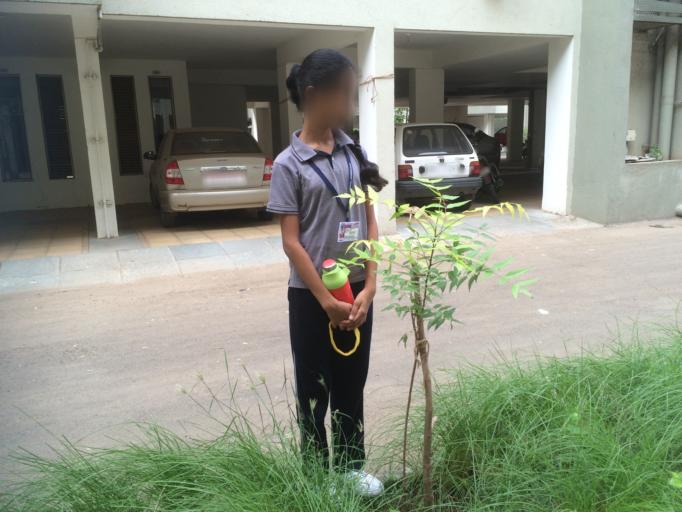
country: IN
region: Gujarat
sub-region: Gandhinagar
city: Adalaj
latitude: 23.1217
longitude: 72.5968
